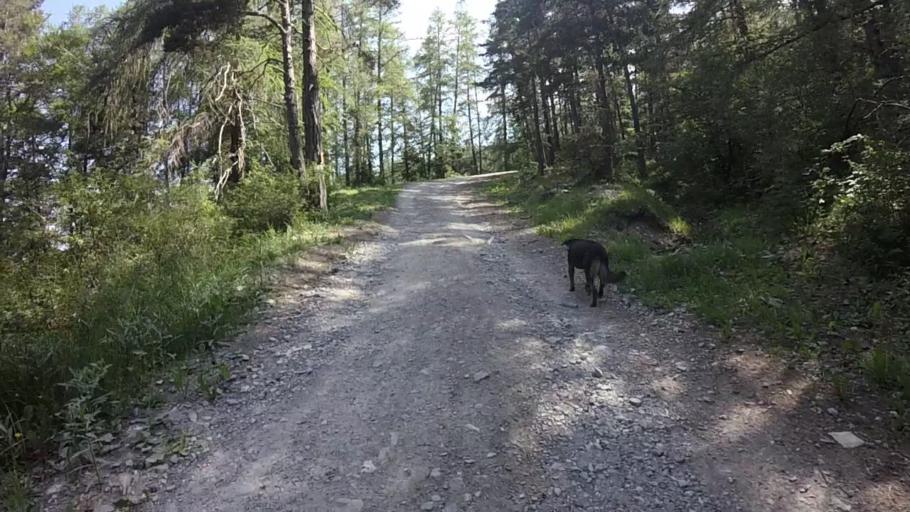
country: FR
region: Provence-Alpes-Cote d'Azur
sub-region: Departement des Alpes-de-Haute-Provence
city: Seyne-les-Alpes
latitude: 44.4046
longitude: 6.3591
